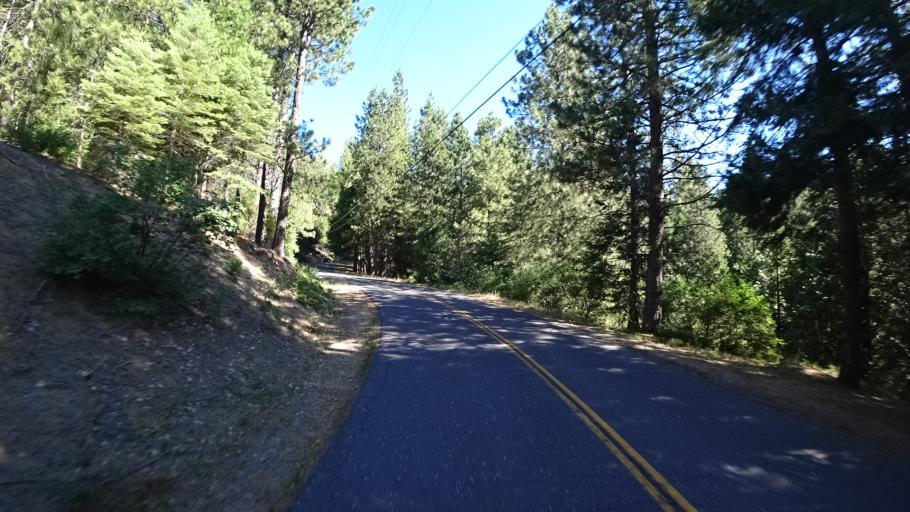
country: US
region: California
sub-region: Calaveras County
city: Arnold
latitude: 38.2900
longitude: -120.2673
